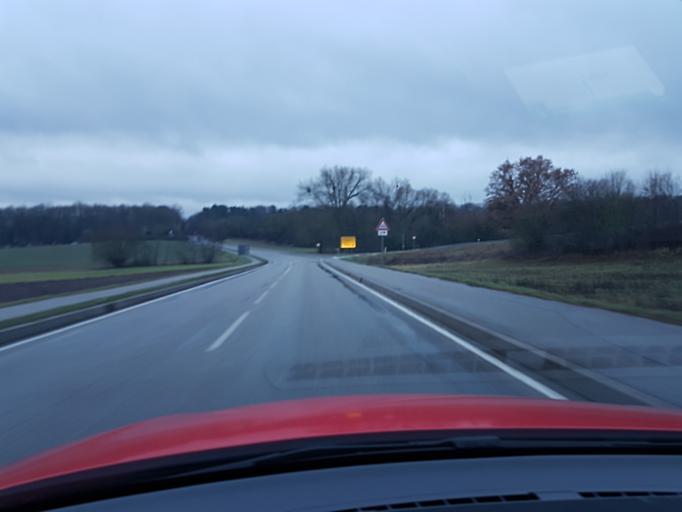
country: DE
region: Baden-Wuerttemberg
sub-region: Karlsruhe Region
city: Muhlacker
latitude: 48.9714
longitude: 8.8602
